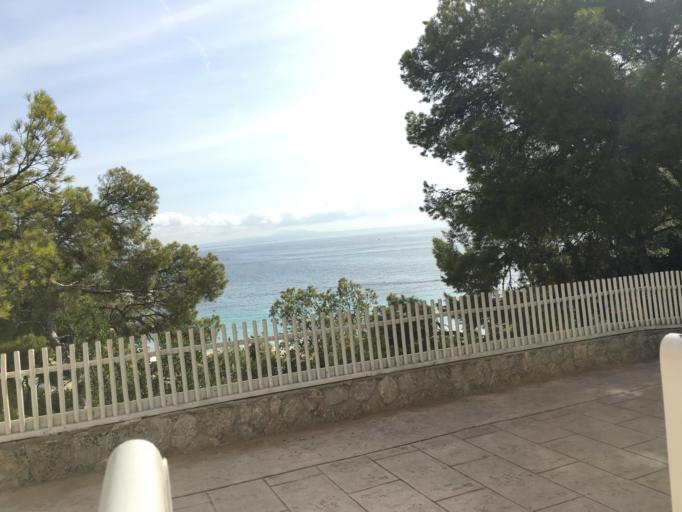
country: ES
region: Balearic Islands
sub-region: Illes Balears
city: Magaluf
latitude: 39.5369
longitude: 2.5895
